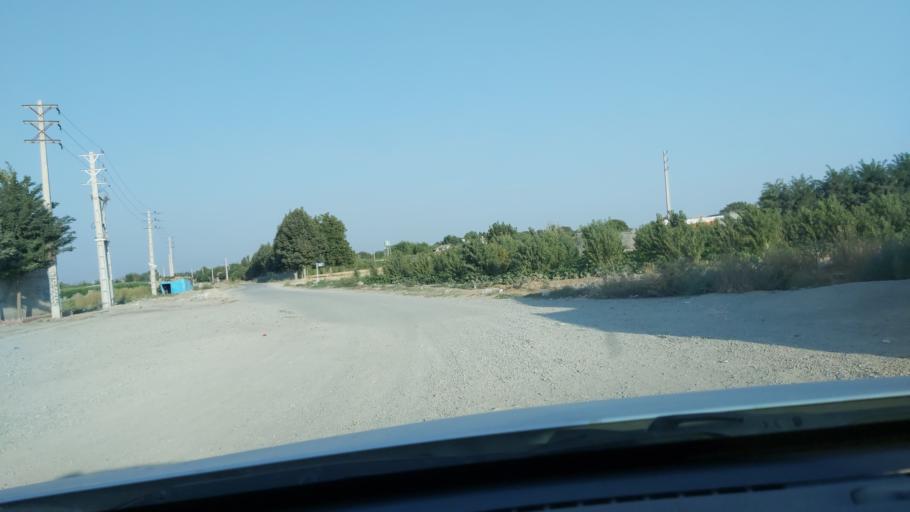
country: IR
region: Alborz
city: Hashtgerd
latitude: 35.8589
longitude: 50.6950
